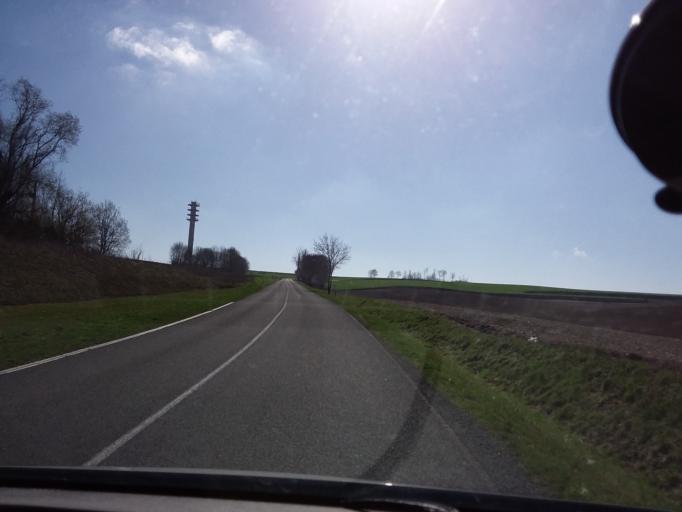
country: FR
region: Picardie
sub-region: Departement de l'Aisne
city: Montcornet
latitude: 49.7187
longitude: 4.0157
